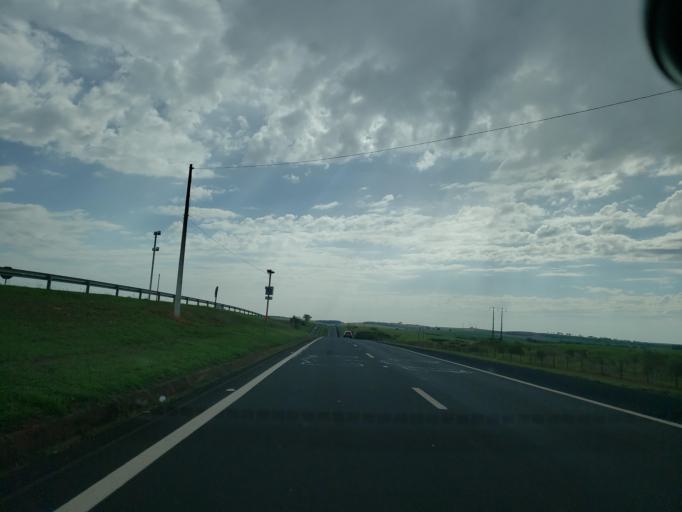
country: BR
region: Sao Paulo
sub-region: Cafelandia
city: Cafelandia
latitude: -21.7550
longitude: -49.6803
